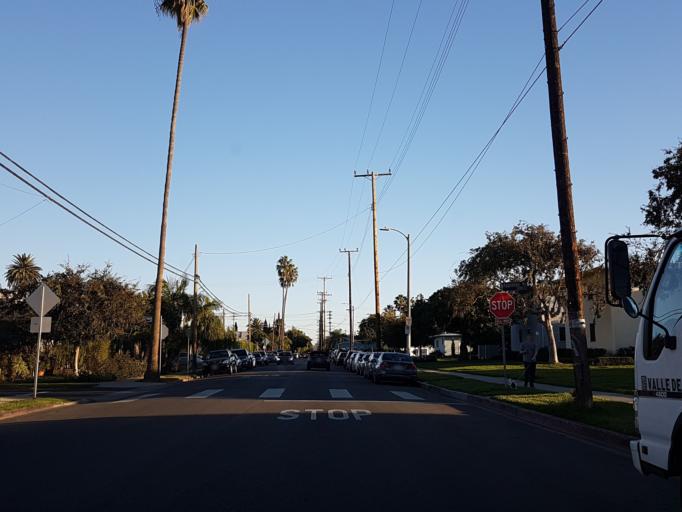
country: US
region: California
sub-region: Los Angeles County
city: Marina del Rey
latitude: 34.0030
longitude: -118.4574
